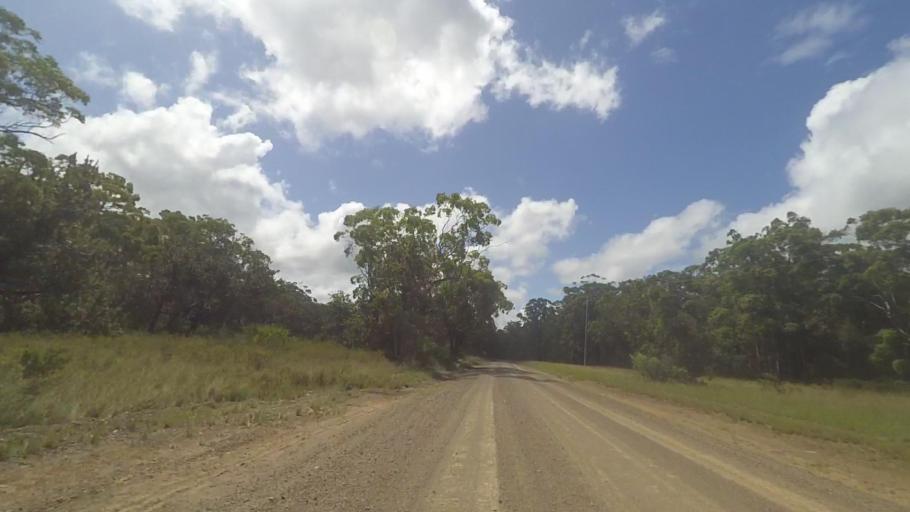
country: AU
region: New South Wales
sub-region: Great Lakes
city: Bulahdelah
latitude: -32.5050
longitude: 152.2912
